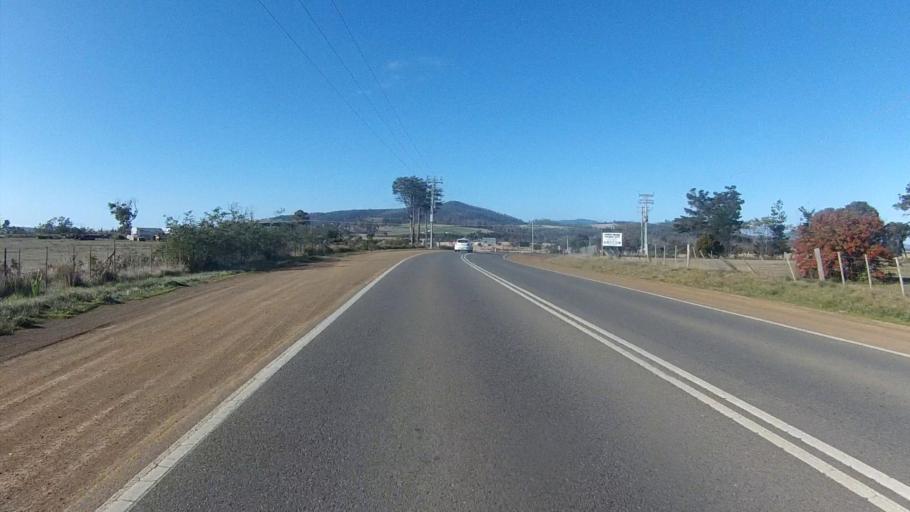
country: AU
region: Tasmania
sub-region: Sorell
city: Sorell
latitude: -42.8923
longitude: 147.8053
